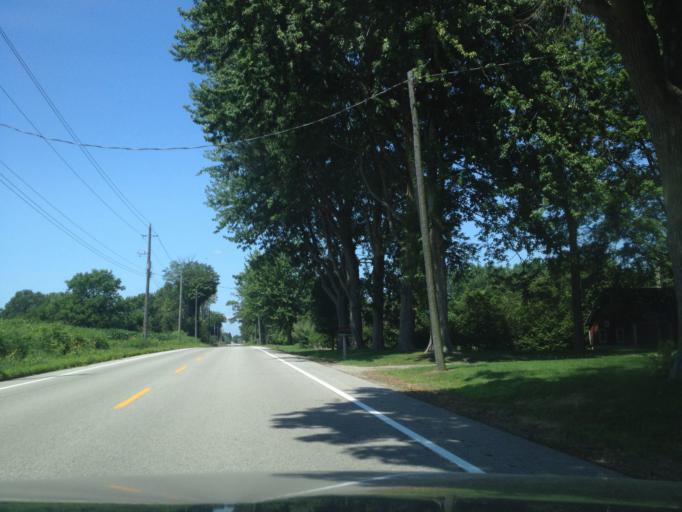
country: CA
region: Ontario
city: Norfolk County
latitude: 42.5885
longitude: -80.6263
